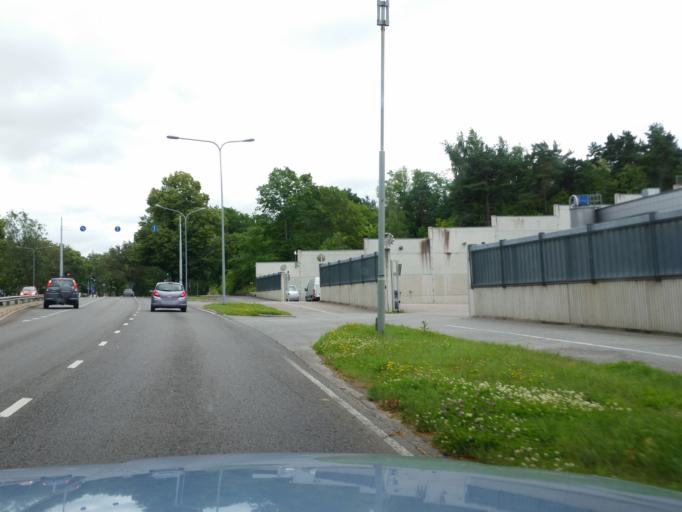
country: FI
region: Varsinais-Suomi
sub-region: Turku
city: Turku
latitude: 60.4423
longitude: 22.2879
